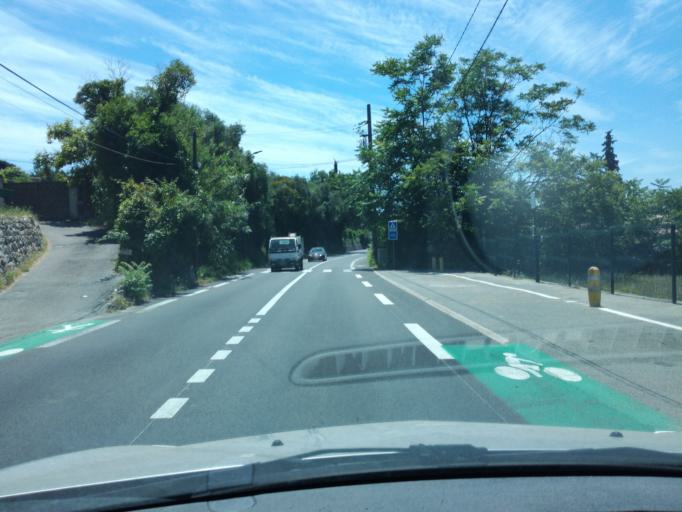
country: FR
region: Provence-Alpes-Cote d'Azur
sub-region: Departement des Alpes-Maritimes
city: Mougins
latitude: 43.5951
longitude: 7.0015
